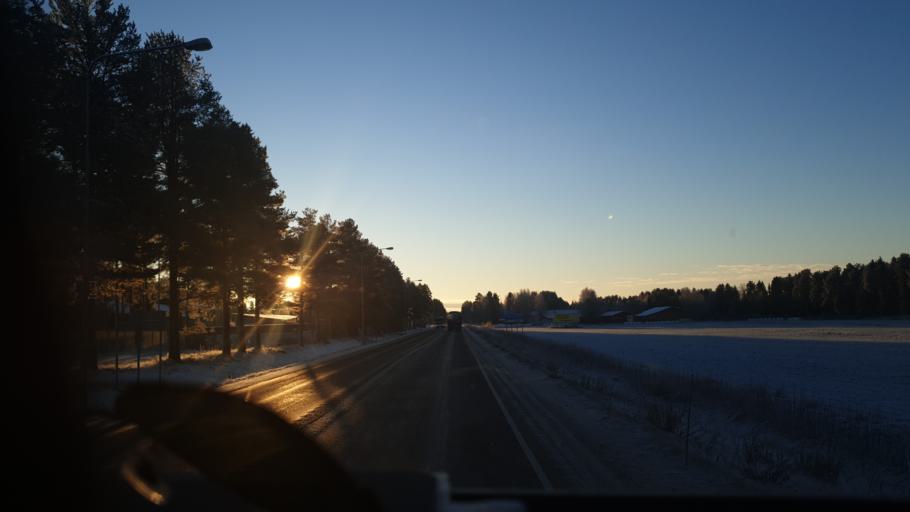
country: FI
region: Northern Ostrobothnia
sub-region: Ylivieska
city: Kalajoki
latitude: 64.2818
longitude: 23.9484
